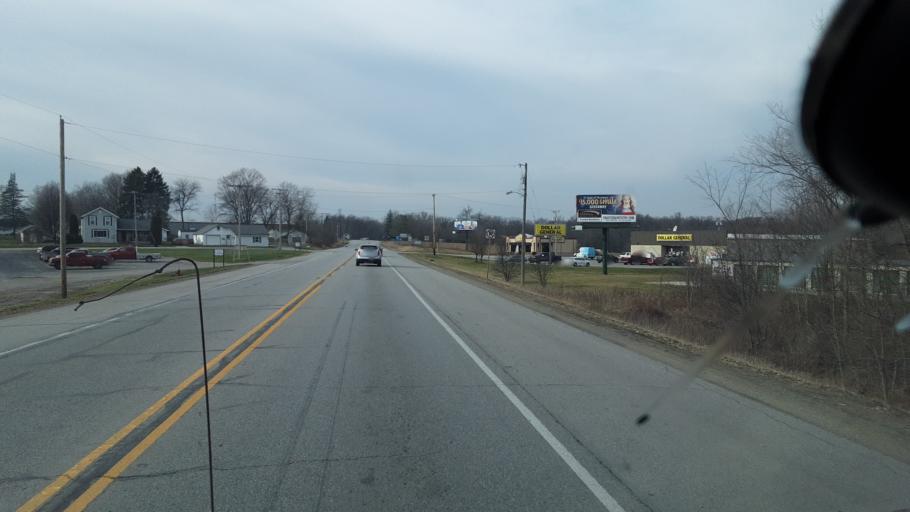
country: US
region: Indiana
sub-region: DeKalb County
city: Waterloo
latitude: 41.4335
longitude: -85.0257
